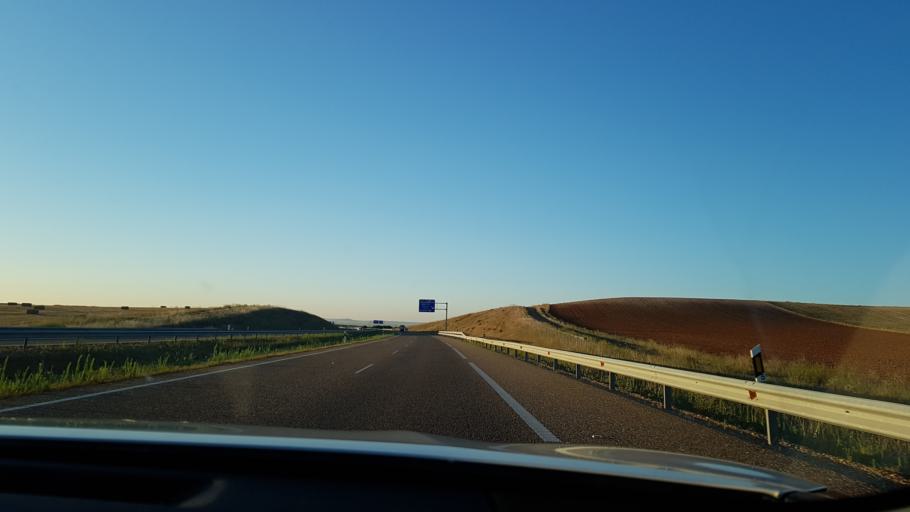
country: ES
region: Castille and Leon
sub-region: Provincia de Zamora
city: Roales
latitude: 41.5651
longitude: -5.7654
